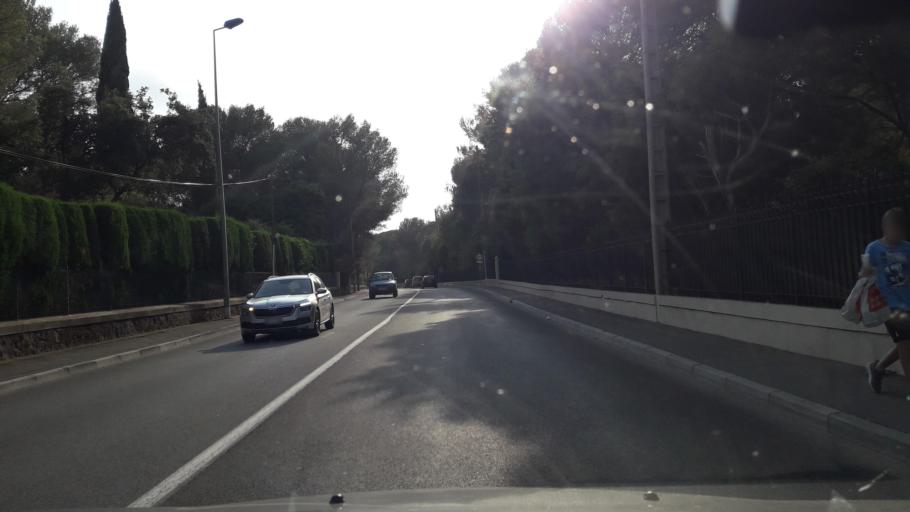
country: FR
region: Provence-Alpes-Cote d'Azur
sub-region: Departement du Var
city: Saint-Raphael
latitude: 43.4169
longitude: 6.8180
